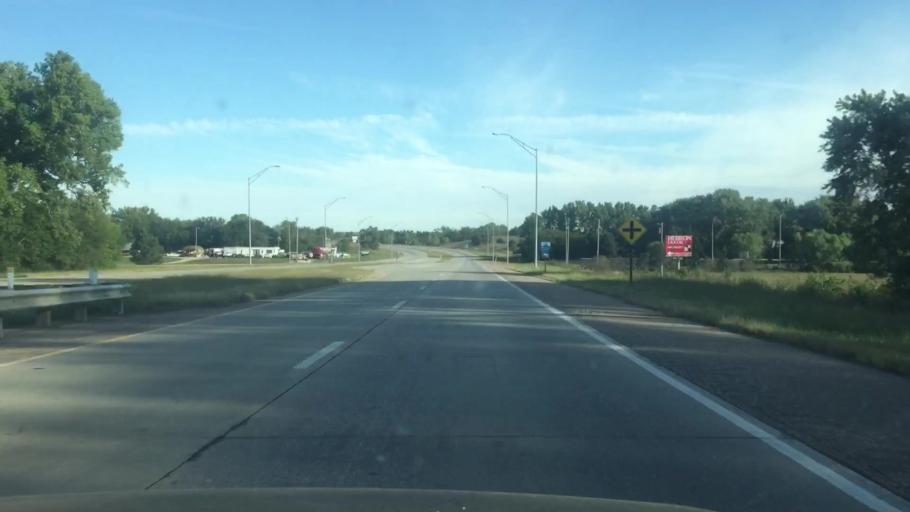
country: US
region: Nebraska
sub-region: Thayer County
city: Hebron
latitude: 40.1598
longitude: -97.5706
